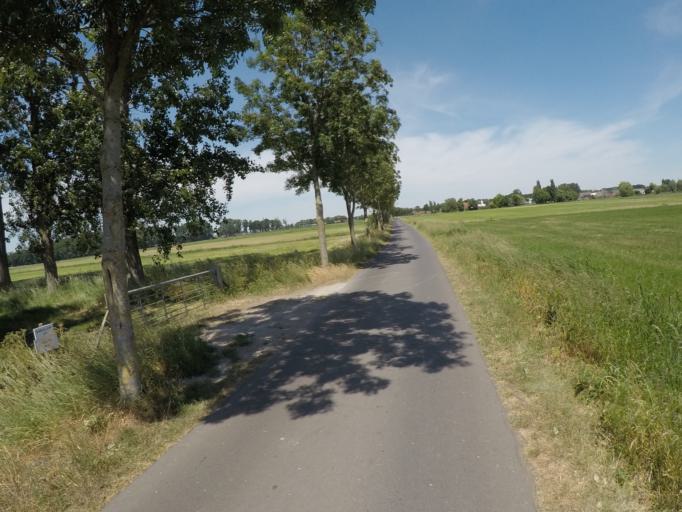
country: BE
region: Flanders
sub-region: Provincie Antwerpen
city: Wuustwezel
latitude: 51.3948
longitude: 4.6258
